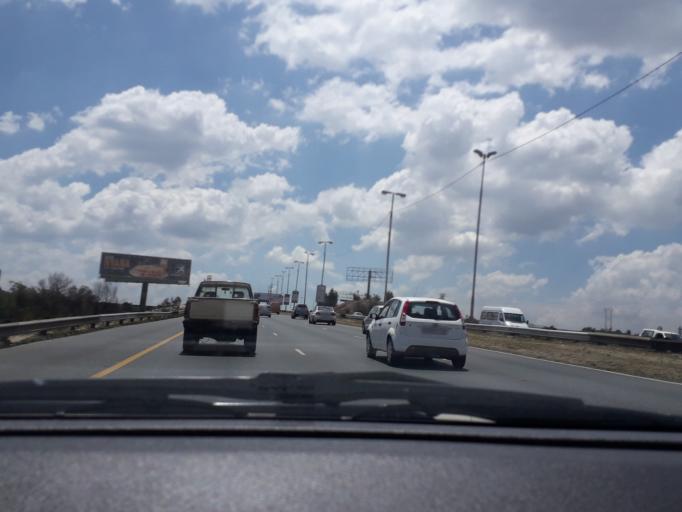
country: ZA
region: Gauteng
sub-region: City of Johannesburg Metropolitan Municipality
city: Johannesburg
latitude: -26.2263
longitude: 28.0193
